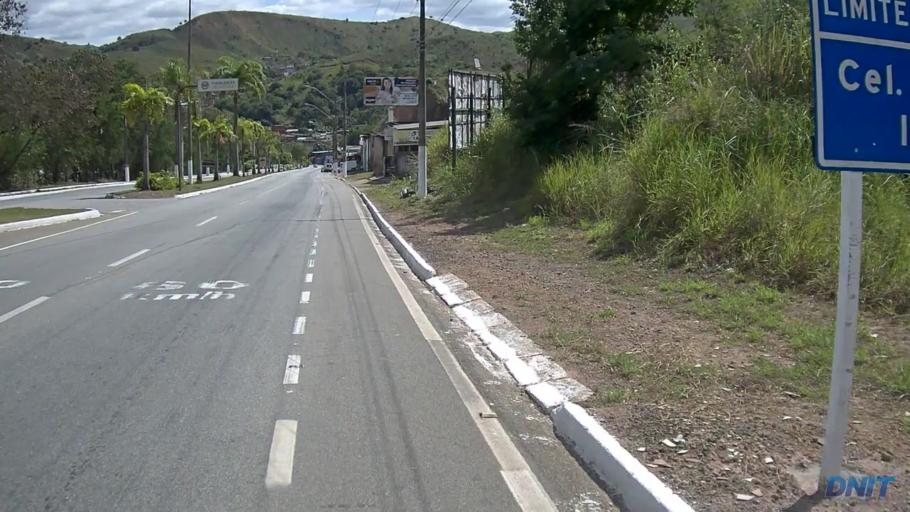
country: BR
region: Minas Gerais
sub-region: Coronel Fabriciano
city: Coronel Fabriciano
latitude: -19.5045
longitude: -42.5953
